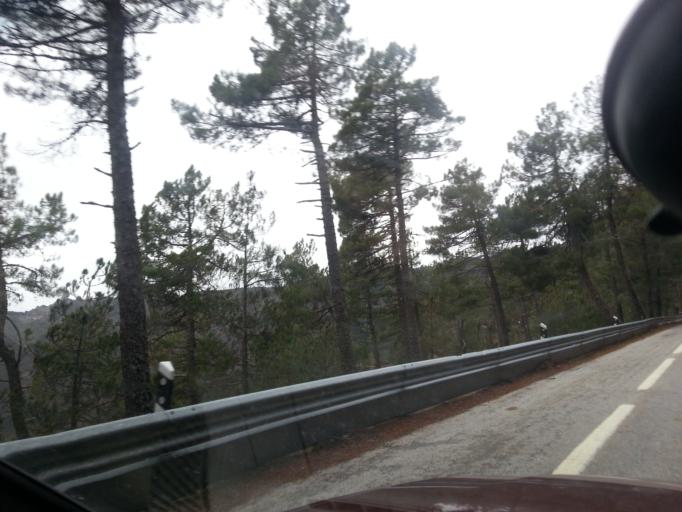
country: PT
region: Guarda
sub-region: Manteigas
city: Manteigas
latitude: 40.4142
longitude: -7.5409
